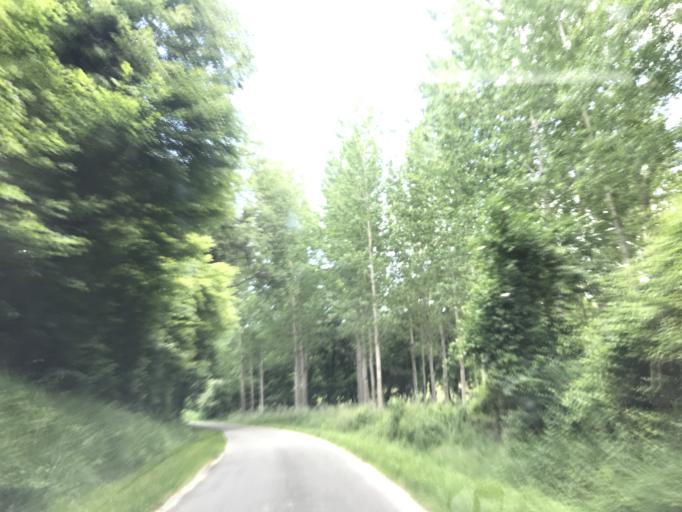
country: FR
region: Aquitaine
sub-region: Departement de la Dordogne
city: Saint-Aulaye
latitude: 45.2642
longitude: 0.1242
